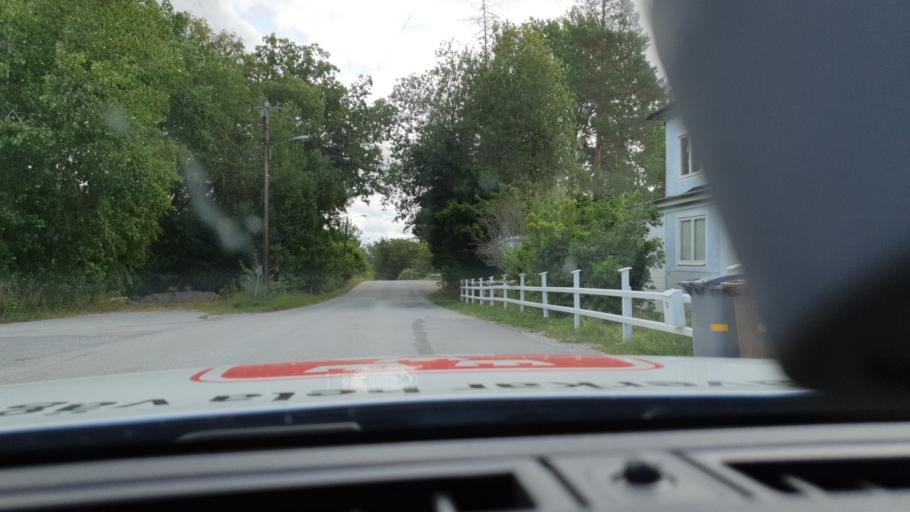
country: SE
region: Stockholm
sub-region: Vaxholms Kommun
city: Vaxholm
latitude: 59.3926
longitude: 18.4147
